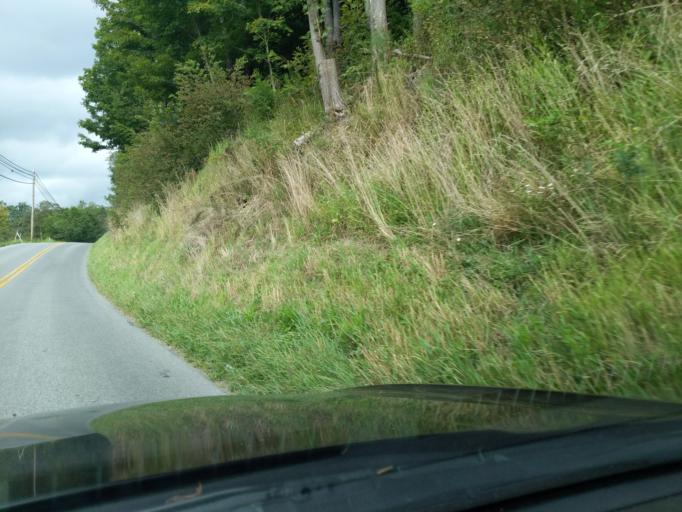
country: US
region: Pennsylvania
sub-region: Blair County
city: Claysburg
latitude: 40.3534
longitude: -78.4564
